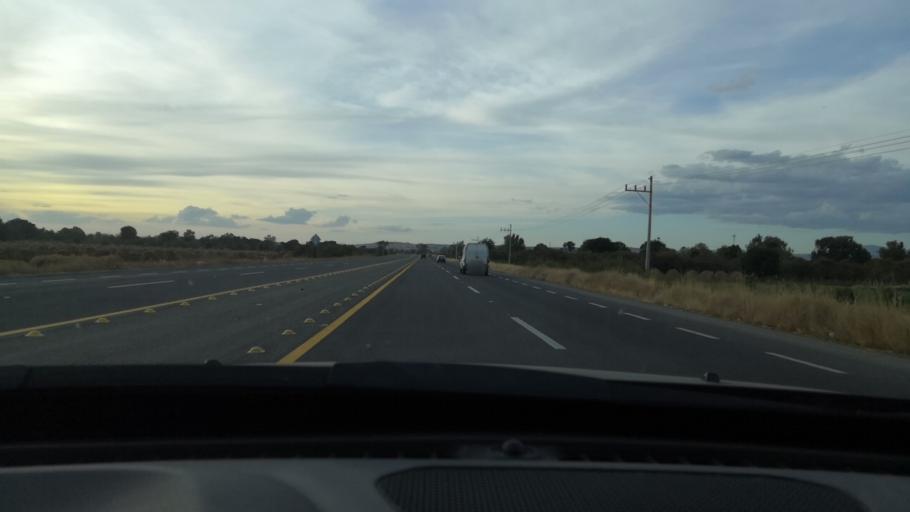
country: MX
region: Guanajuato
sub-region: Silao de la Victoria
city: Loma de Yerbabuena
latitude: 21.0243
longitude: -101.4406
